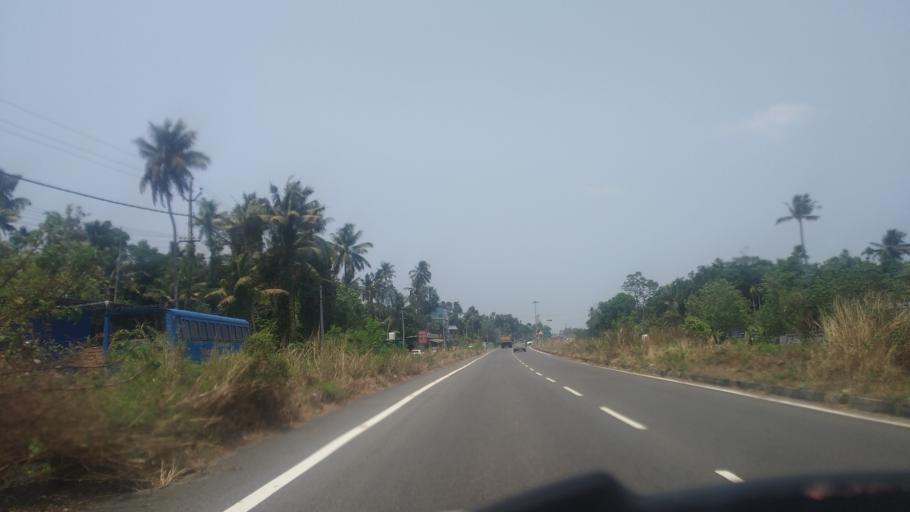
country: IN
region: Kerala
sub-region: Thrissur District
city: Kodungallur
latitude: 10.2189
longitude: 76.1961
